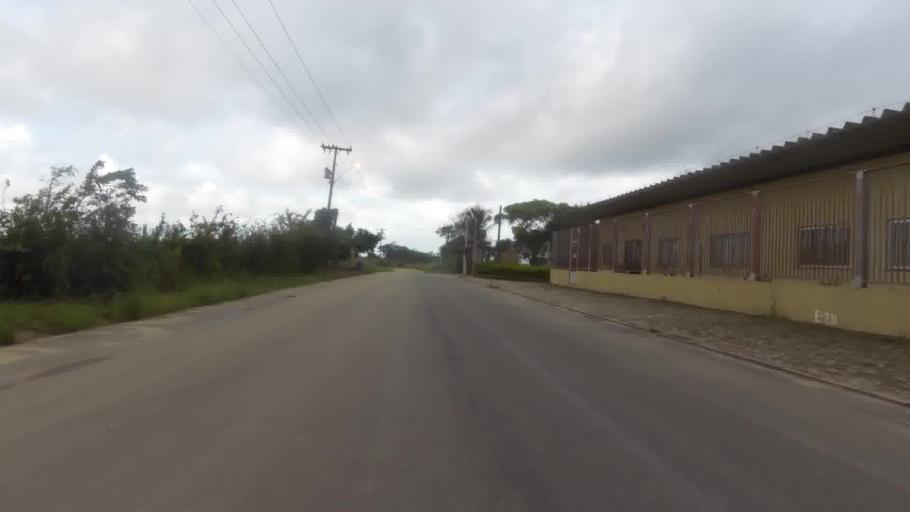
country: BR
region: Espirito Santo
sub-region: Piuma
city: Piuma
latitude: -20.7726
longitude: -40.6303
